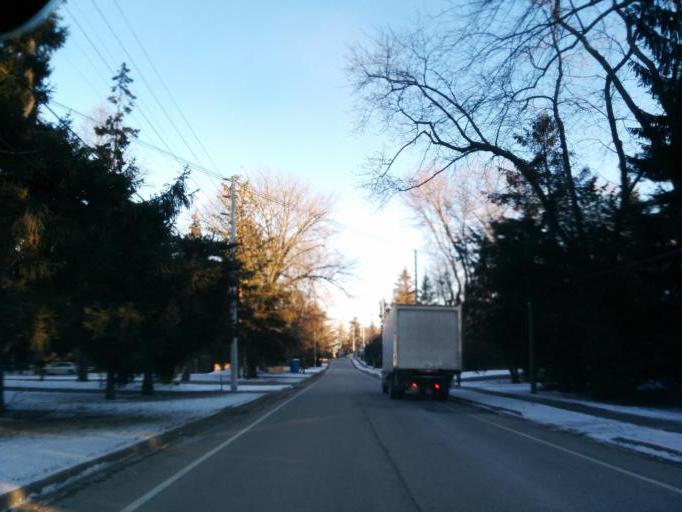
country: CA
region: Ontario
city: Mississauga
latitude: 43.5485
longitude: -79.6115
